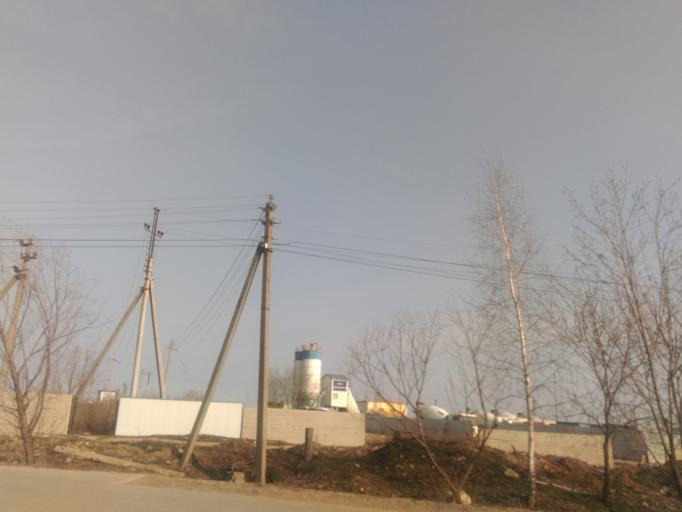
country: RU
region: Moskovskaya
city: Kokoshkino
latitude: 55.5794
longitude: 37.1496
